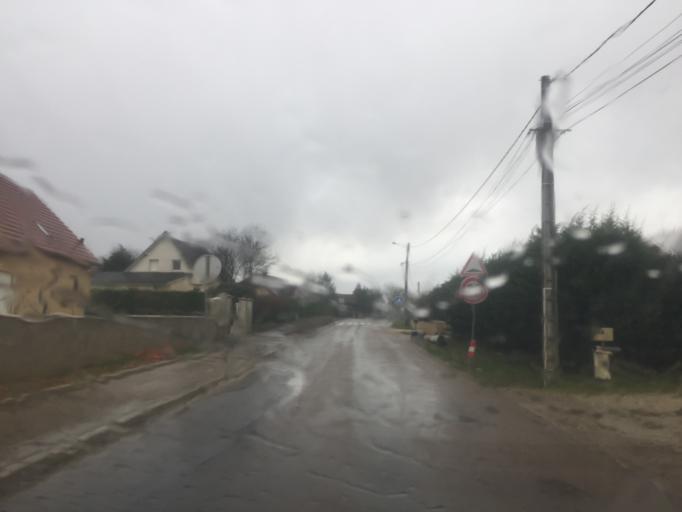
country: FR
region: Franche-Comte
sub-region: Departement du Jura
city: Dampierre
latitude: 47.2127
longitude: 5.7262
